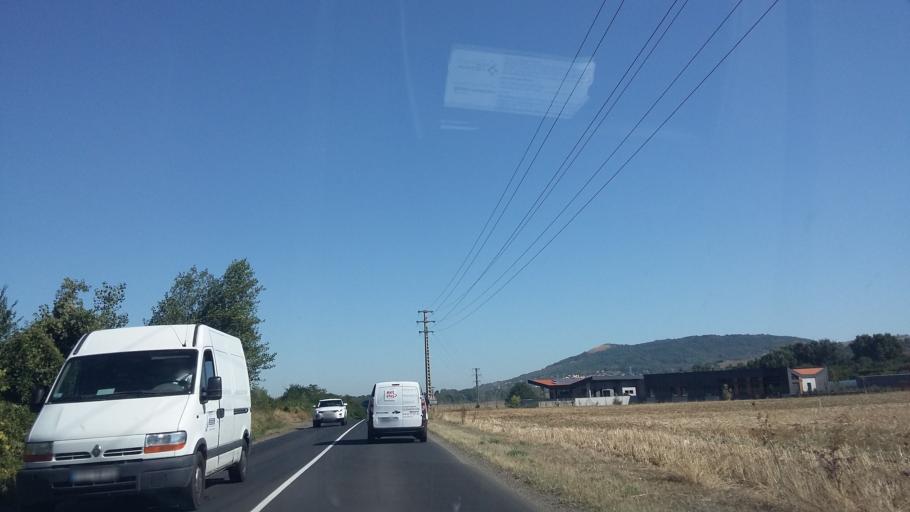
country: FR
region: Auvergne
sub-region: Departement du Puy-de-Dome
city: Perignat-sur-Allier
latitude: 45.7238
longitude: 3.2248
